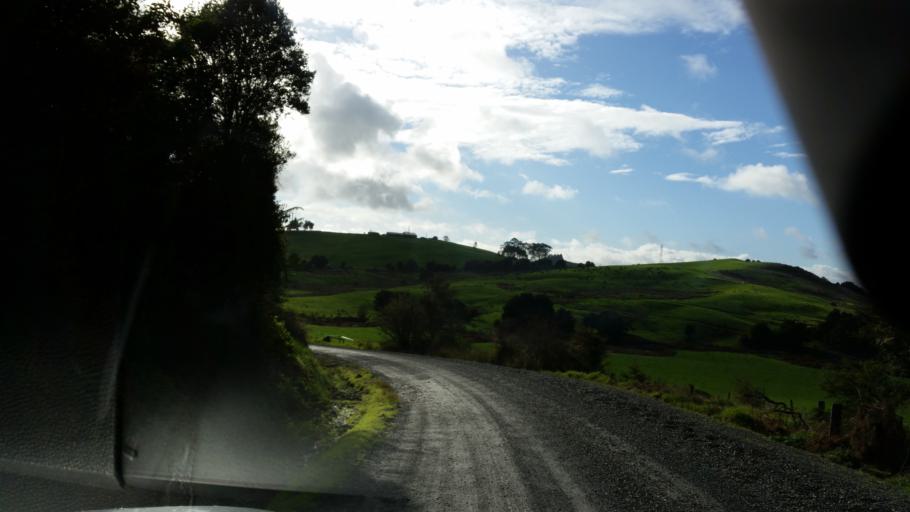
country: NZ
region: Northland
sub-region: Whangarei
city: Maungatapere
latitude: -35.6968
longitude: 174.1034
